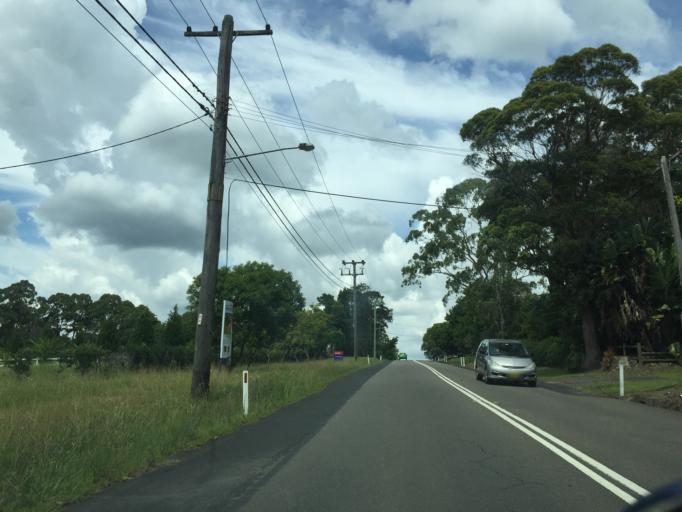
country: AU
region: New South Wales
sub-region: Hornsby Shire
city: Galston
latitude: -33.6754
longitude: 151.0328
